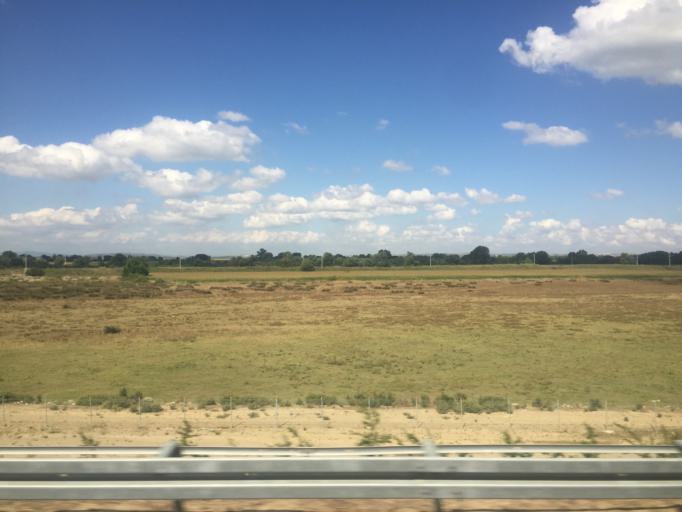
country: TR
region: Bursa
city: Tatkavakli
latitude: 40.1151
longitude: 28.2776
